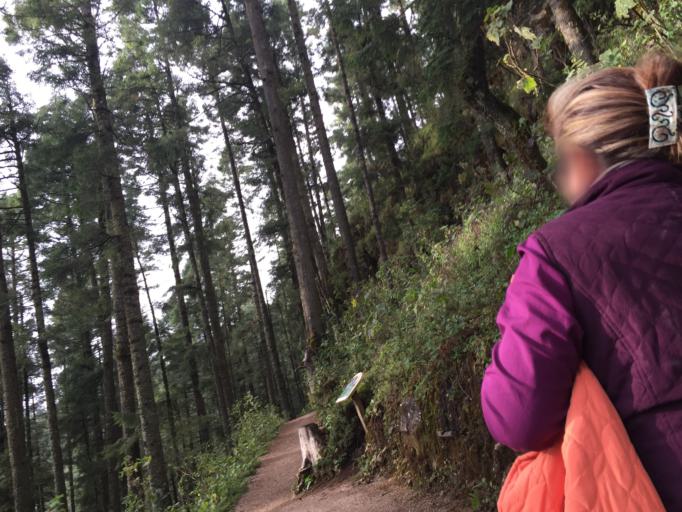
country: MX
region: Michoacan
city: Mineral de Angangueo
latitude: 19.6714
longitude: -100.2896
